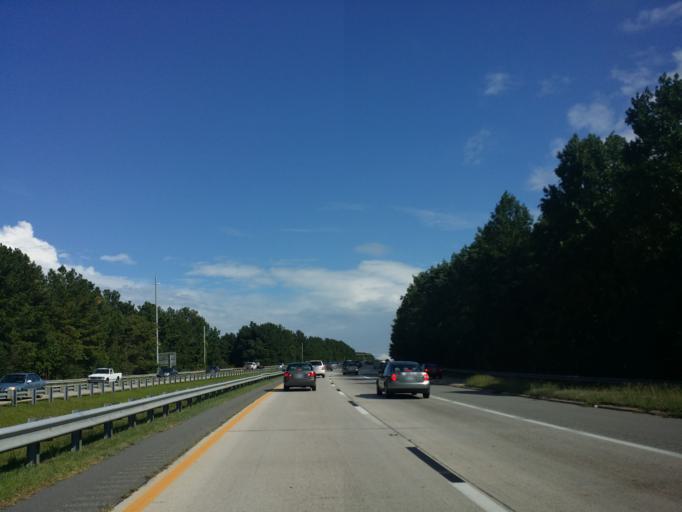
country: US
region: North Carolina
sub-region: Durham County
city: Durham
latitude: 35.9742
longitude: -78.8722
